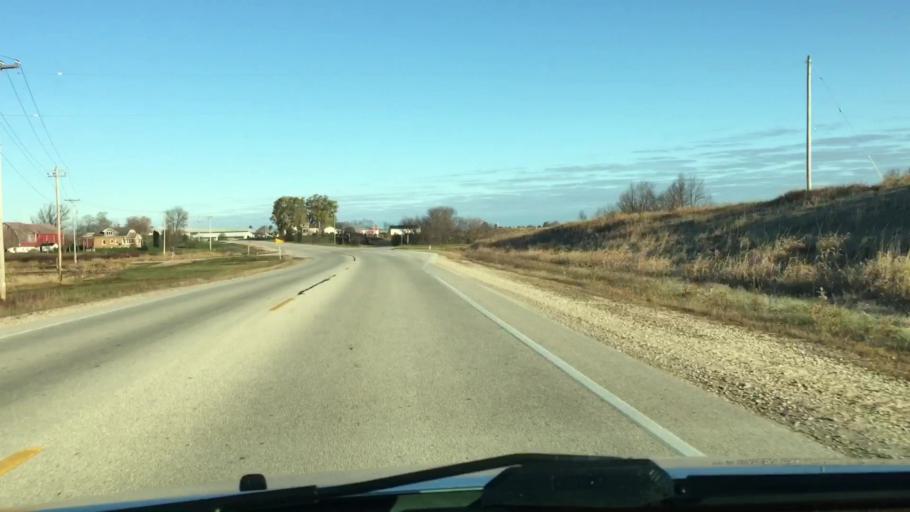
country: US
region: Wisconsin
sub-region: Dodge County
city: Lomira
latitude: 43.5643
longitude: -88.4468
